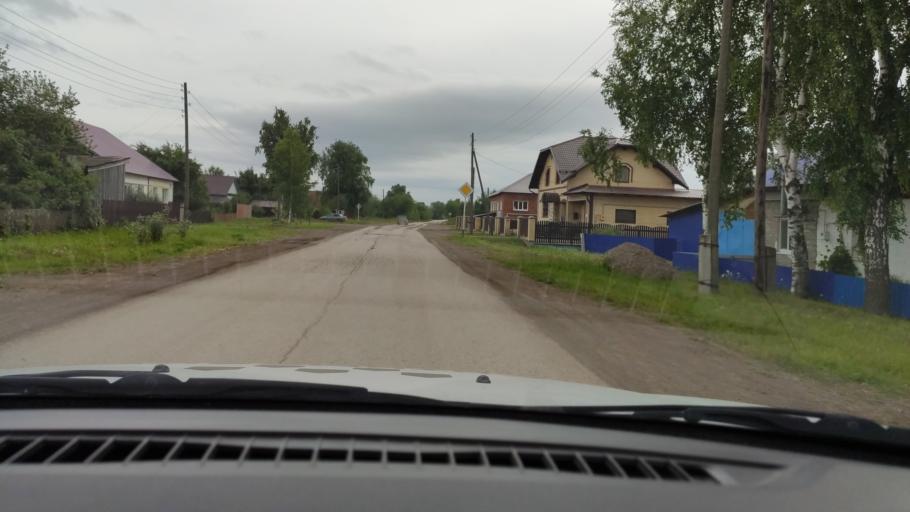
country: RU
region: Perm
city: Orda
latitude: 57.2979
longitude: 56.6546
